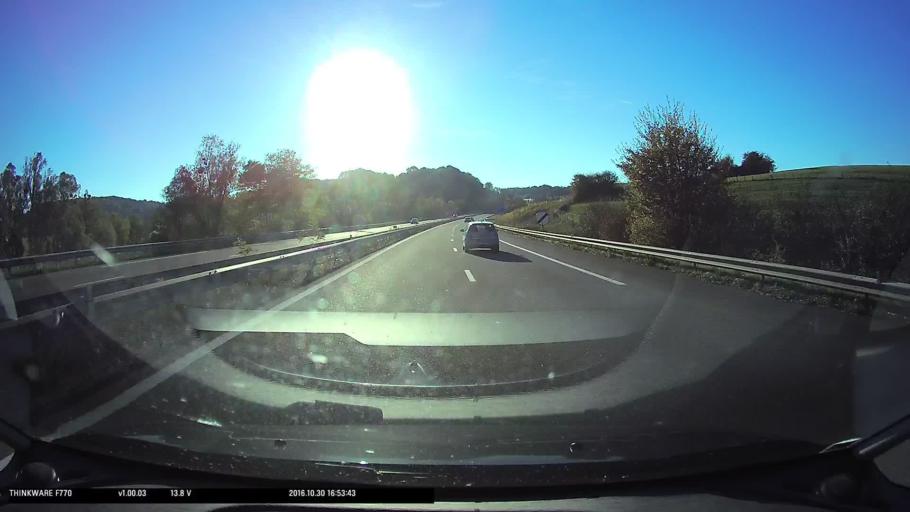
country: FR
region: Franche-Comte
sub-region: Departement du Doubs
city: Chemaudin
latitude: 47.2215
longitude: 5.8773
